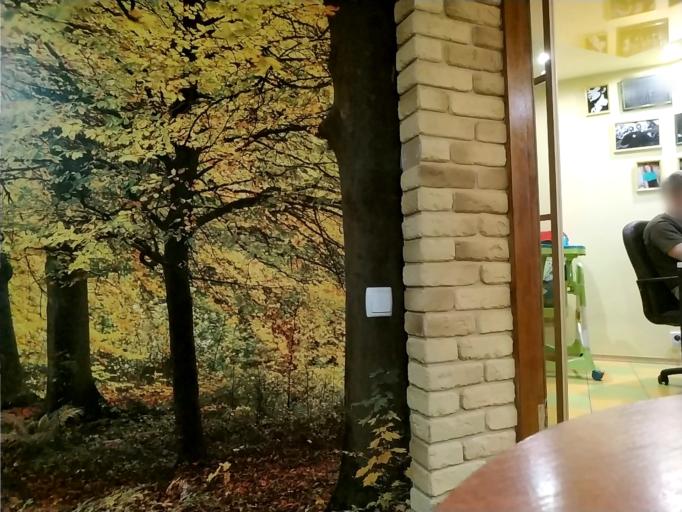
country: RU
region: Tverskaya
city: Zapadnaya Dvina
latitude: 56.3282
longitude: 31.8979
